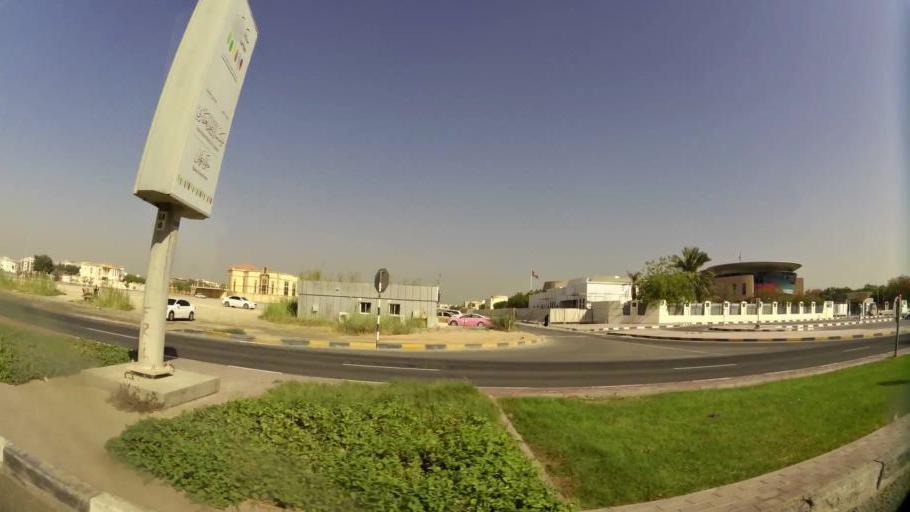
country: AE
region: Ajman
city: Ajman
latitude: 25.4065
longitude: 55.5074
